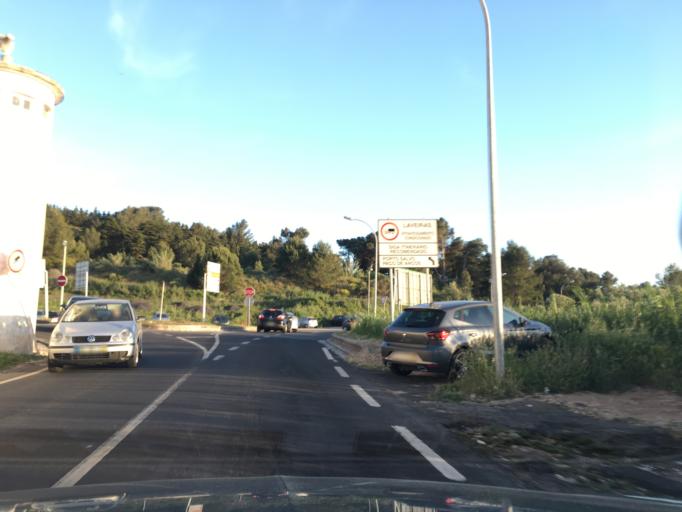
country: PT
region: Lisbon
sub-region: Oeiras
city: Quejas
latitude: 38.7082
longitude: -9.2703
